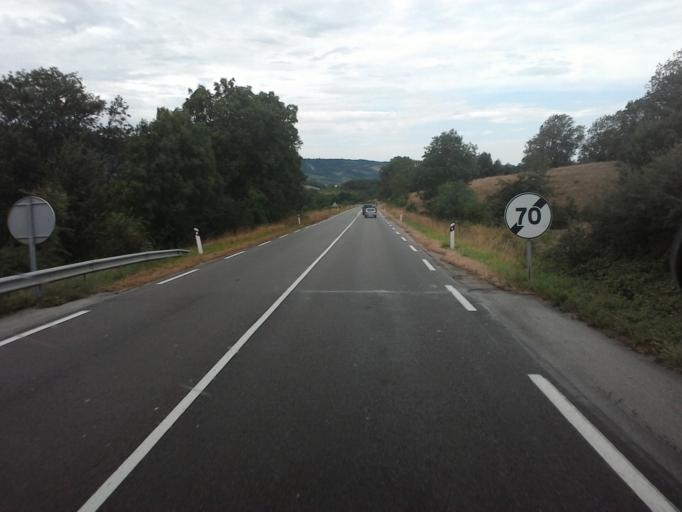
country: FR
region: Franche-Comte
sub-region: Departement du Jura
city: Poligny
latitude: 46.8634
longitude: 5.7143
